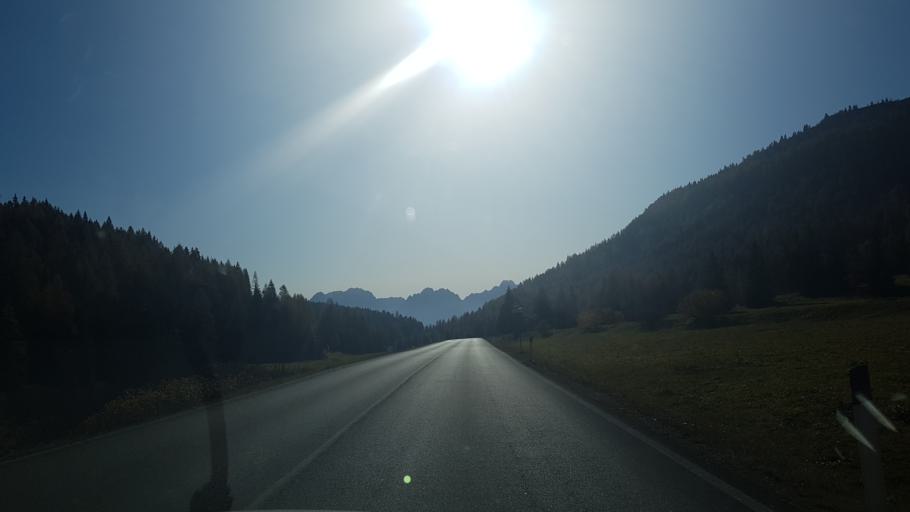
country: IT
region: Trentino-Alto Adige
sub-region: Bolzano
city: Sesto
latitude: 46.6553
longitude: 12.4212
